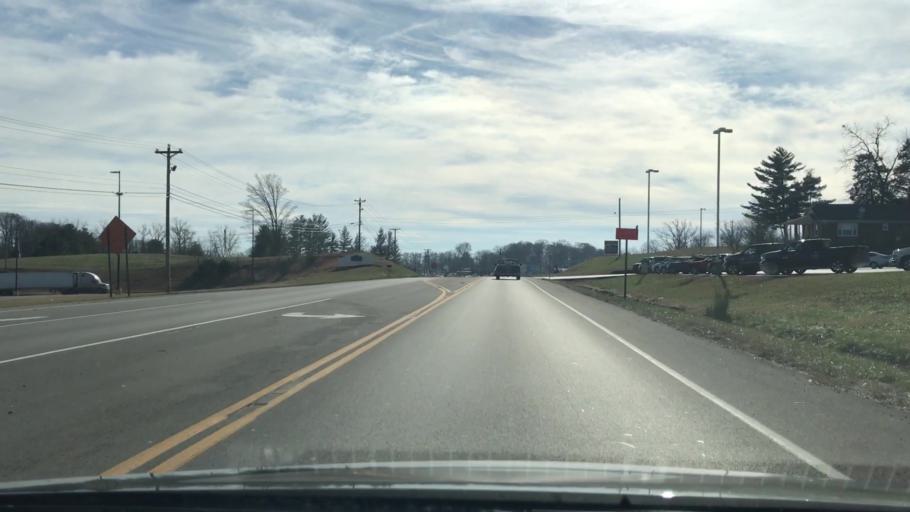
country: US
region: Kentucky
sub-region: Monroe County
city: Tompkinsville
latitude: 36.7243
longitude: -85.6875
